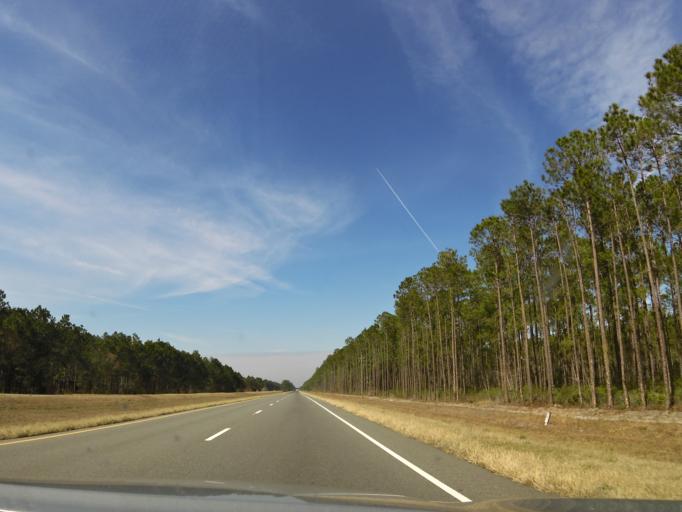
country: US
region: Georgia
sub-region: Ware County
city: Waycross
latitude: 31.0903
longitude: -82.2181
